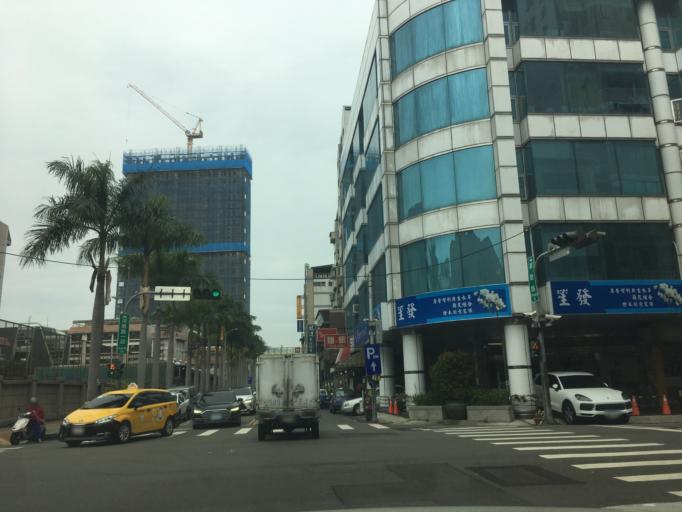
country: TW
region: Taiwan
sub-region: Taichung City
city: Taichung
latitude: 24.1699
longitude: 120.6623
